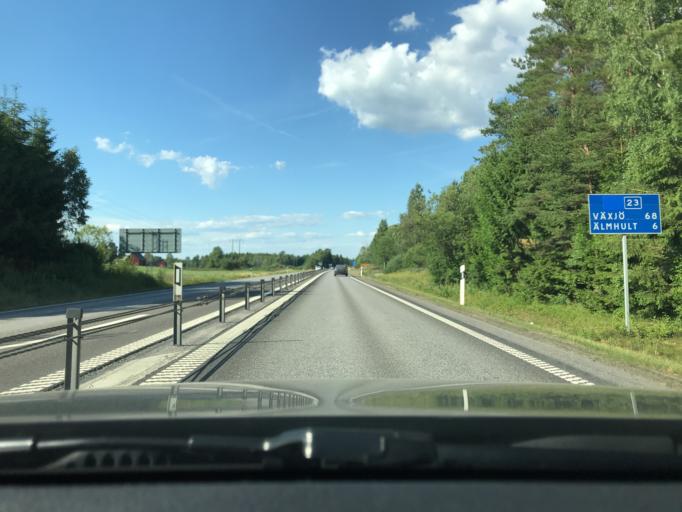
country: SE
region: Kronoberg
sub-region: Almhults Kommun
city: AElmhult
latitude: 56.5021
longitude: 14.1237
